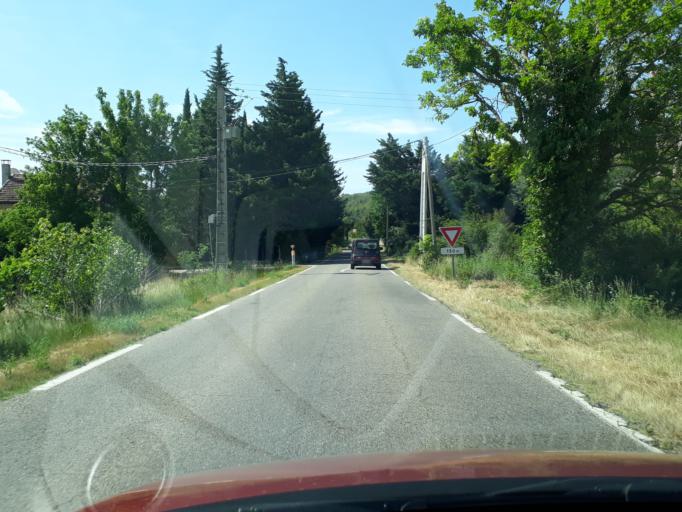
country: FR
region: Provence-Alpes-Cote d'Azur
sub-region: Departement du Vaucluse
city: Sarrians
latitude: 44.1047
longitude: 4.9841
